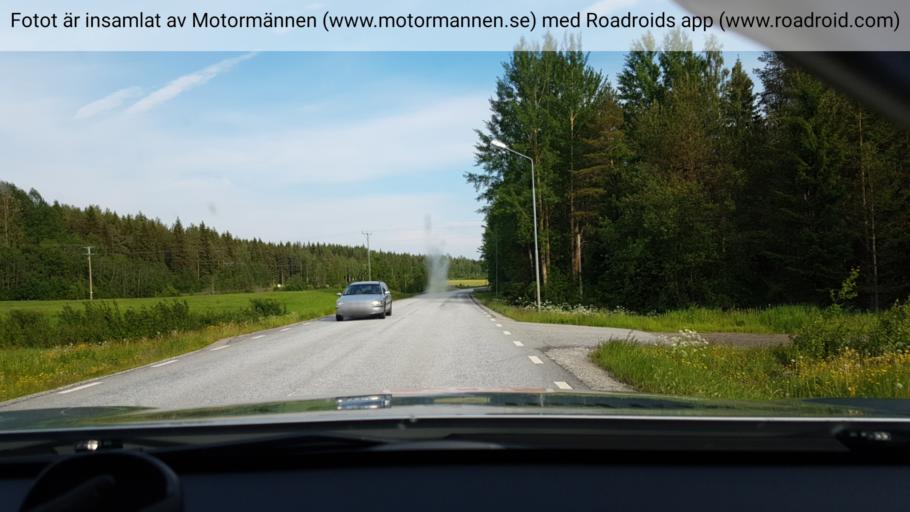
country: SE
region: Vaesterbotten
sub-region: Vindelns Kommun
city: Vindeln
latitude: 64.1241
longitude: 19.5571
